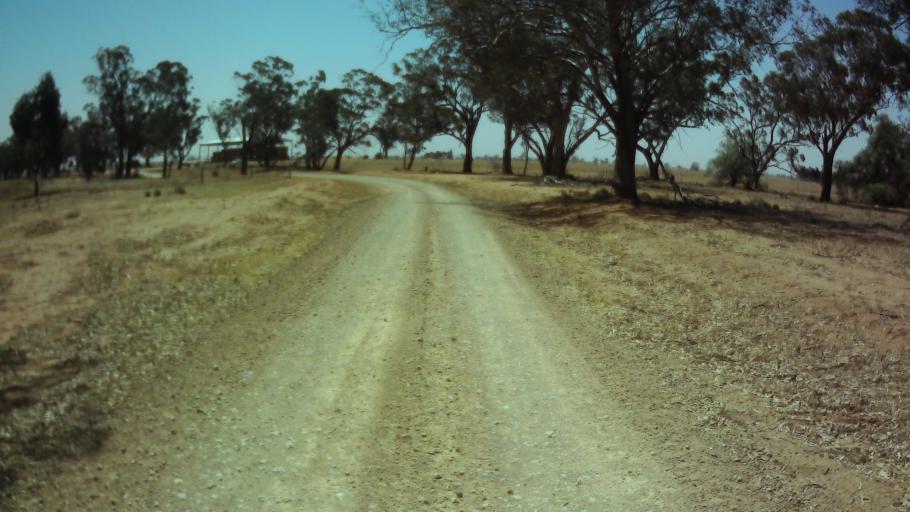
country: AU
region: New South Wales
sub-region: Weddin
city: Grenfell
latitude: -34.0149
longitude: 147.8971
